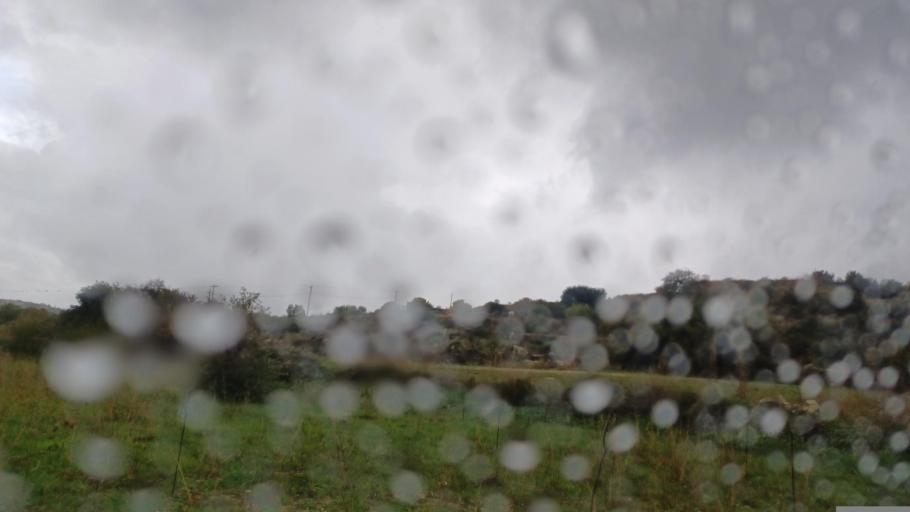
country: CY
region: Pafos
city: Mesogi
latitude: 34.8681
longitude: 32.5432
